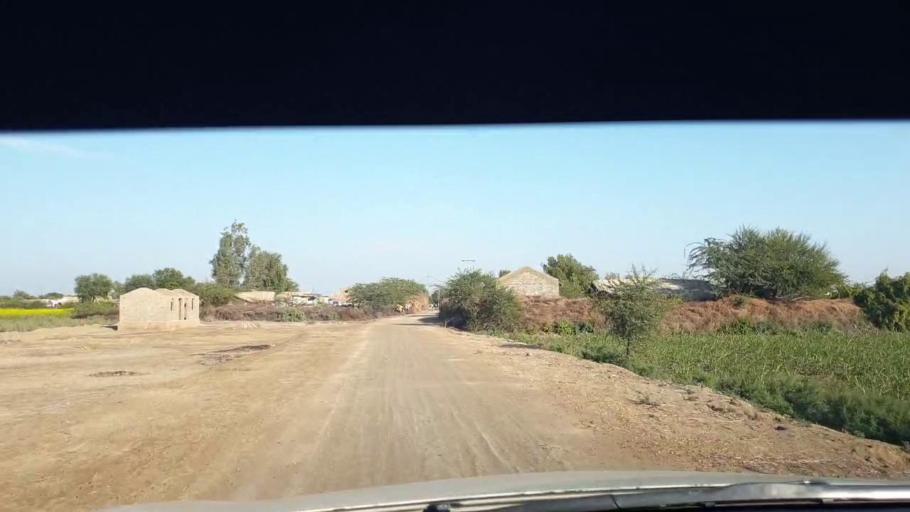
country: PK
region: Sindh
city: Berani
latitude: 25.7900
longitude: 68.9330
